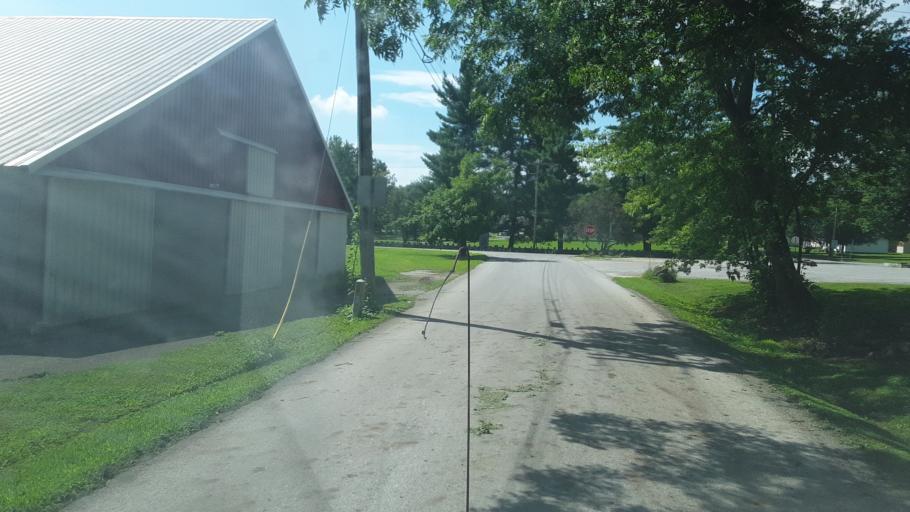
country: US
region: Kentucky
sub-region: Todd County
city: Elkton
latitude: 36.8442
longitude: -87.3008
